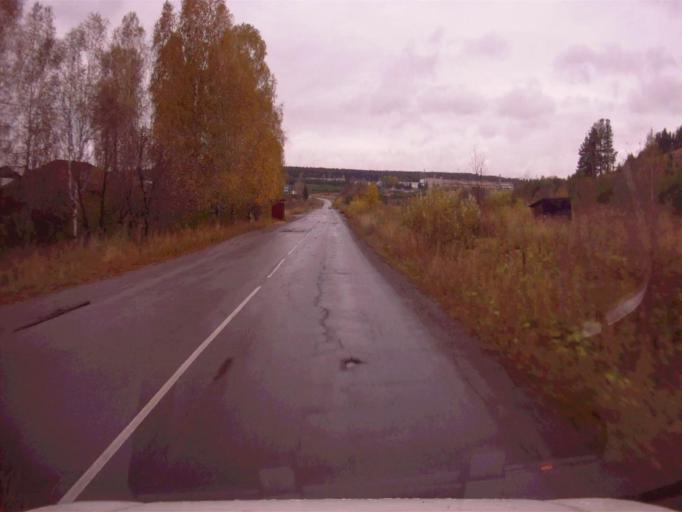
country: RU
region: Chelyabinsk
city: Verkhniy Ufaley
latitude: 56.0604
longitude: 60.1917
